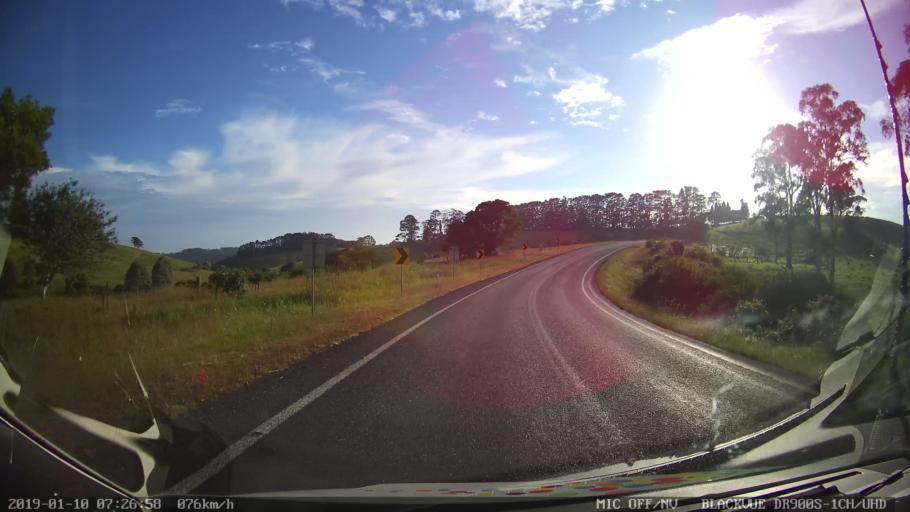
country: AU
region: New South Wales
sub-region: Bellingen
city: Dorrigo
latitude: -30.3703
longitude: 152.6076
